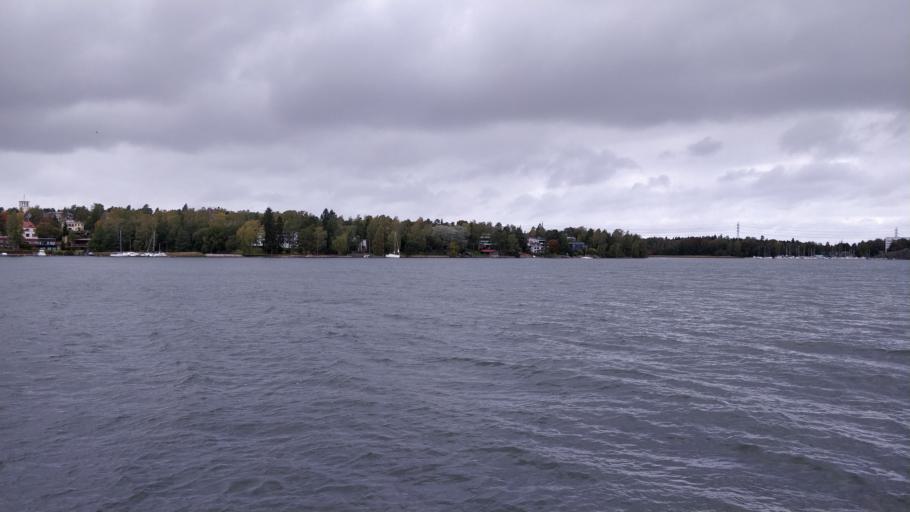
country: FI
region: Uusimaa
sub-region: Helsinki
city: Helsinki
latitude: 60.1813
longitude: 25.0230
